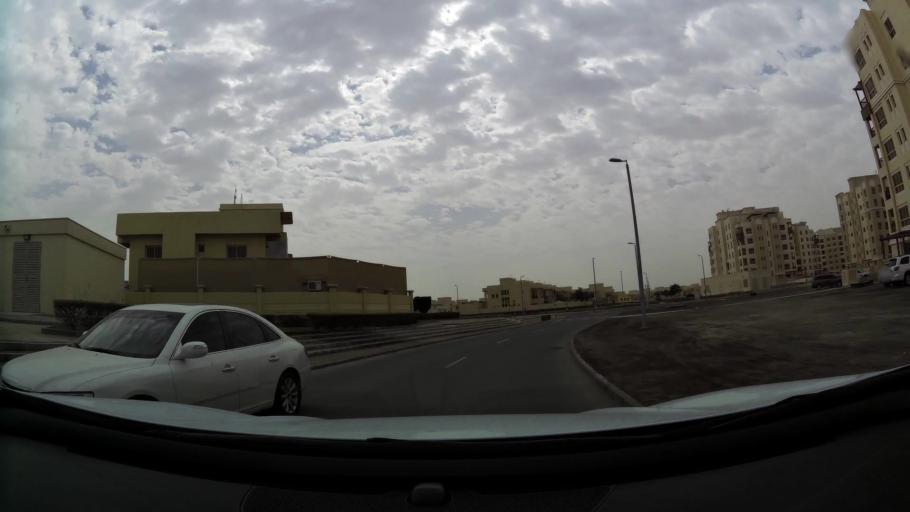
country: AE
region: Abu Dhabi
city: Abu Dhabi
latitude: 24.3130
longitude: 54.6241
